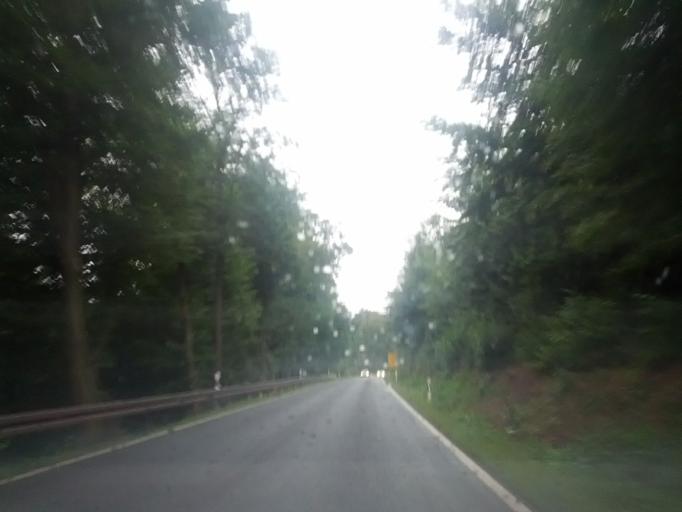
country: DE
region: Thuringia
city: Tabarz
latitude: 50.8912
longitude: 10.4916
